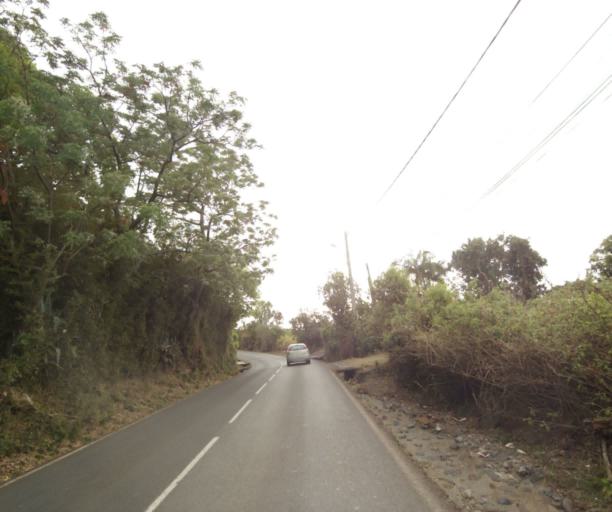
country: RE
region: Reunion
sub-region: Reunion
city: Saint-Paul
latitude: -21.0374
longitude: 55.2956
